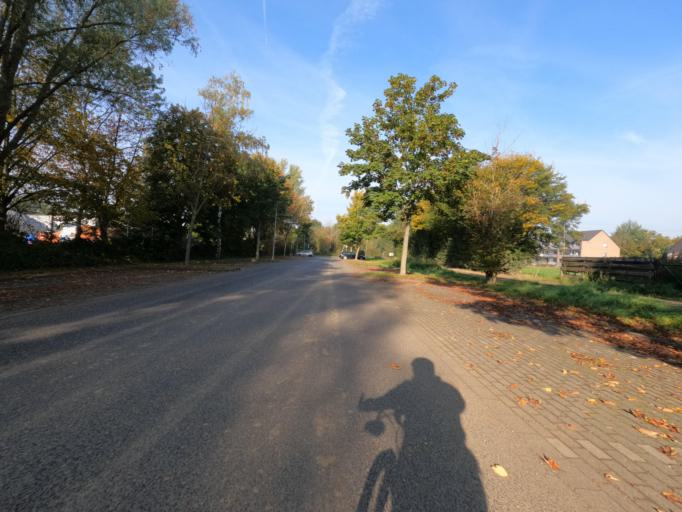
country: DE
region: North Rhine-Westphalia
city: Huckelhoven
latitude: 51.0342
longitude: 6.2713
